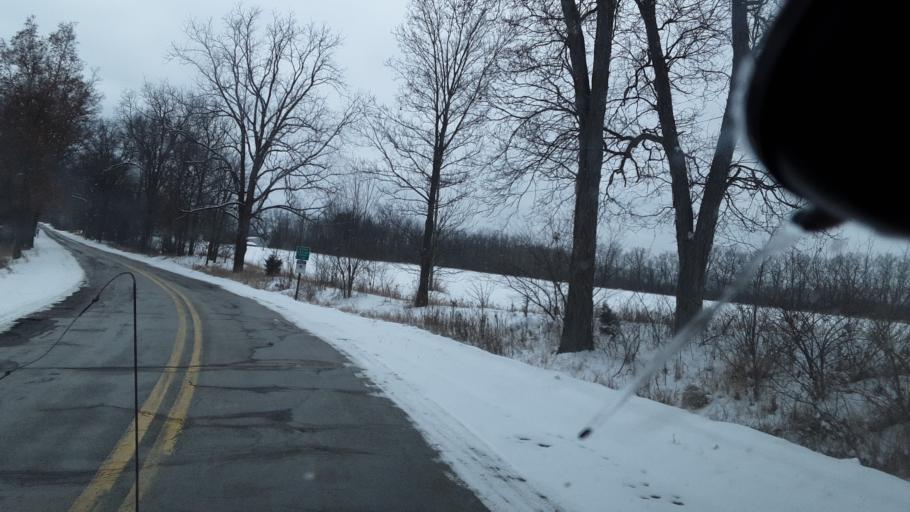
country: US
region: Michigan
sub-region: Ingham County
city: Leslie
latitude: 42.5093
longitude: -84.3891
